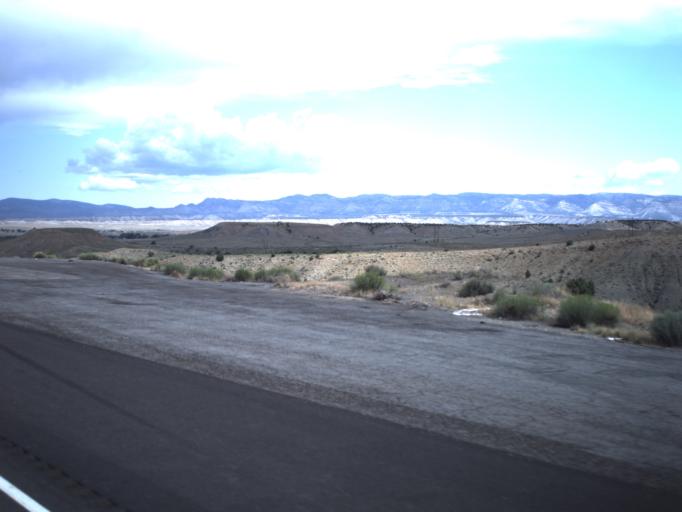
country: US
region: Utah
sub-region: Carbon County
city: Wellington
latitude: 39.5498
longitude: -110.6536
